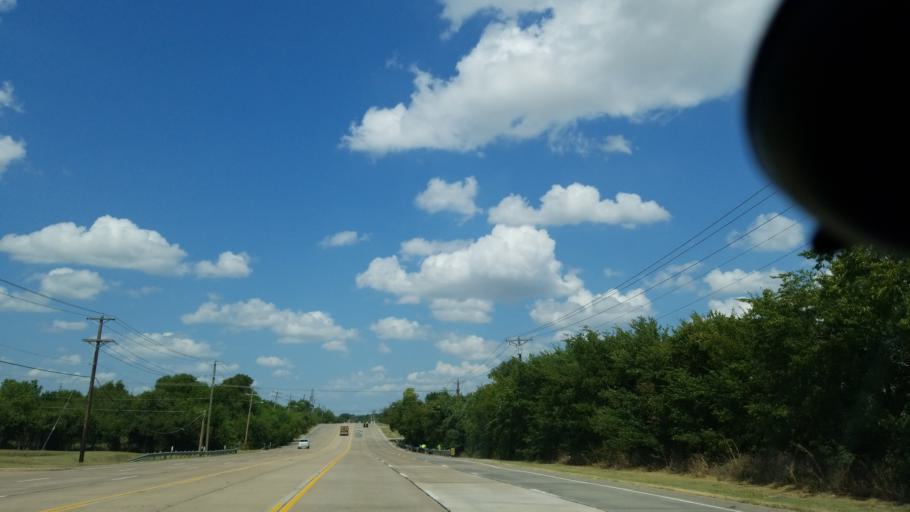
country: US
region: Texas
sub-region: Dallas County
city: Grand Prairie
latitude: 32.7238
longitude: -96.9941
